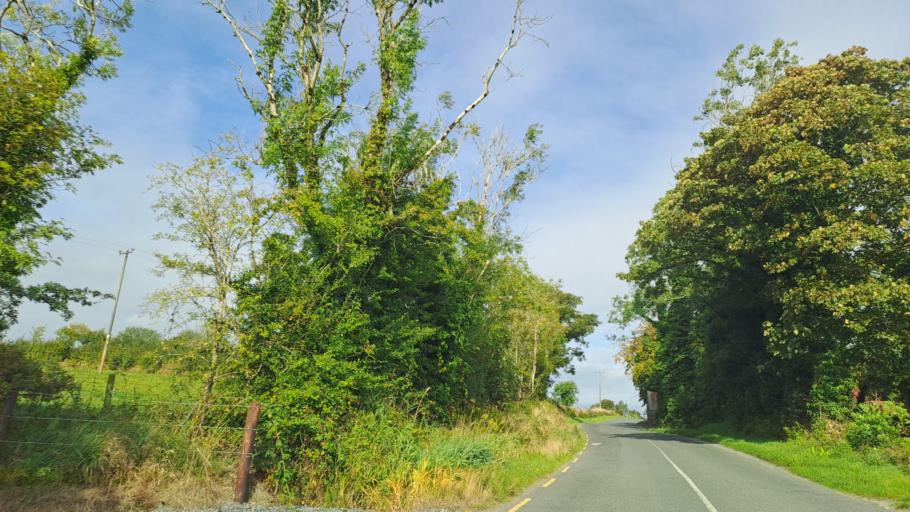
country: IE
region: Ulster
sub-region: An Cabhan
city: Kingscourt
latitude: 53.9540
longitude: -6.8422
